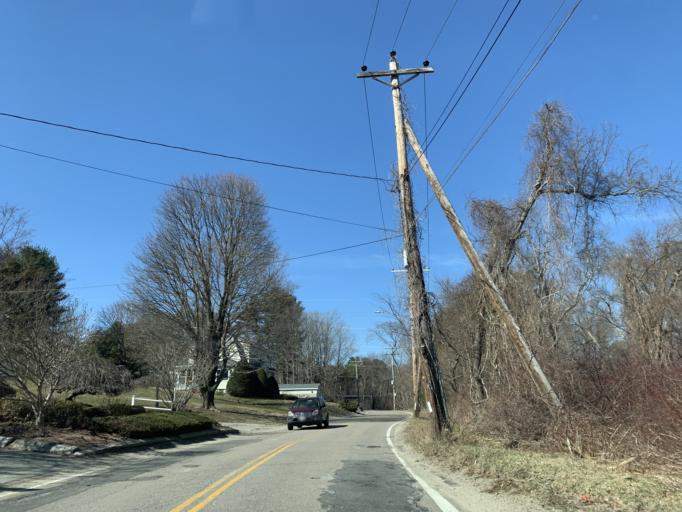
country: US
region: Massachusetts
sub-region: Norfolk County
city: Sharon
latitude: 42.1379
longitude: -71.1723
